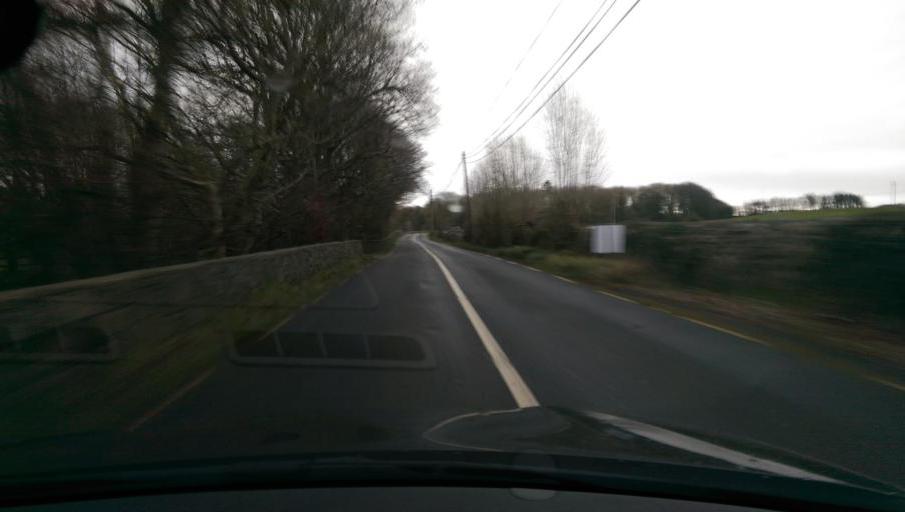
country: IE
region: Connaught
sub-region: County Galway
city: Athenry
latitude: 53.3077
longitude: -8.7881
